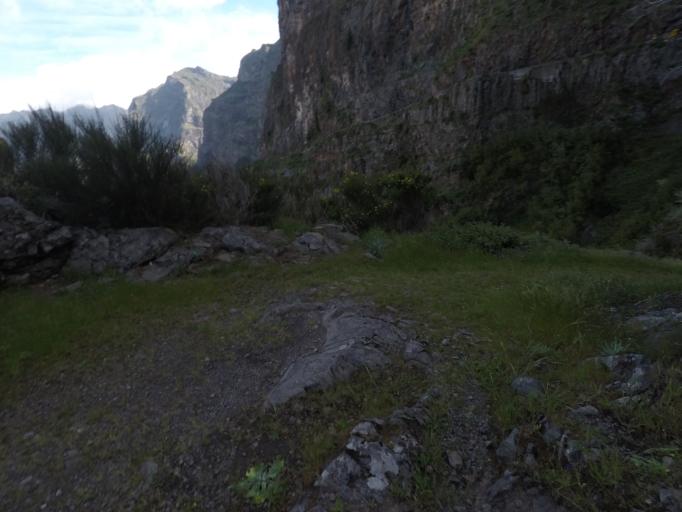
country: PT
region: Madeira
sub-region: Camara de Lobos
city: Curral das Freiras
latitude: 32.7122
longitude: -16.9639
